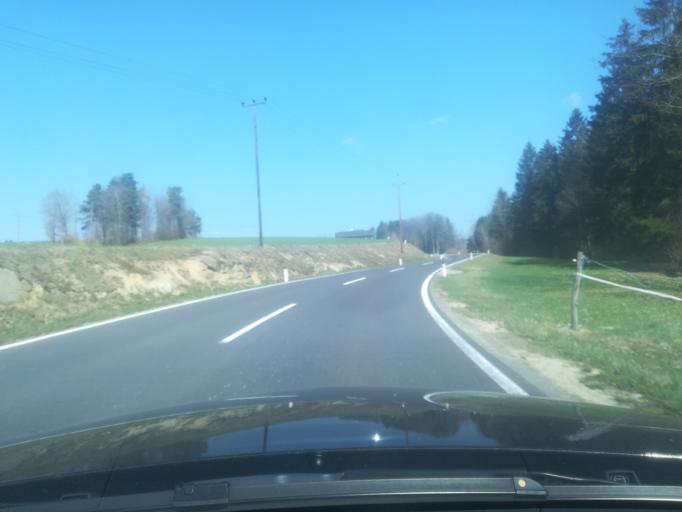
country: AT
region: Upper Austria
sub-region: Politischer Bezirk Perg
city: Perg
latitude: 48.3630
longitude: 14.6806
